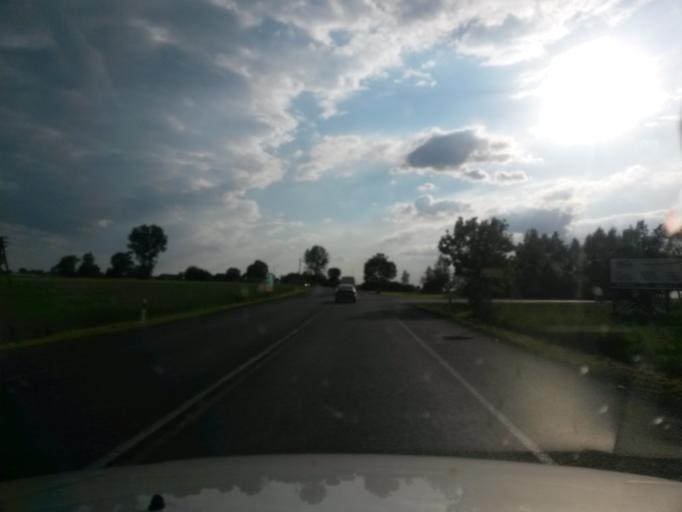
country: PL
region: Lodz Voivodeship
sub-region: Powiat piotrkowski
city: Grabica
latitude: 51.4220
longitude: 19.4934
